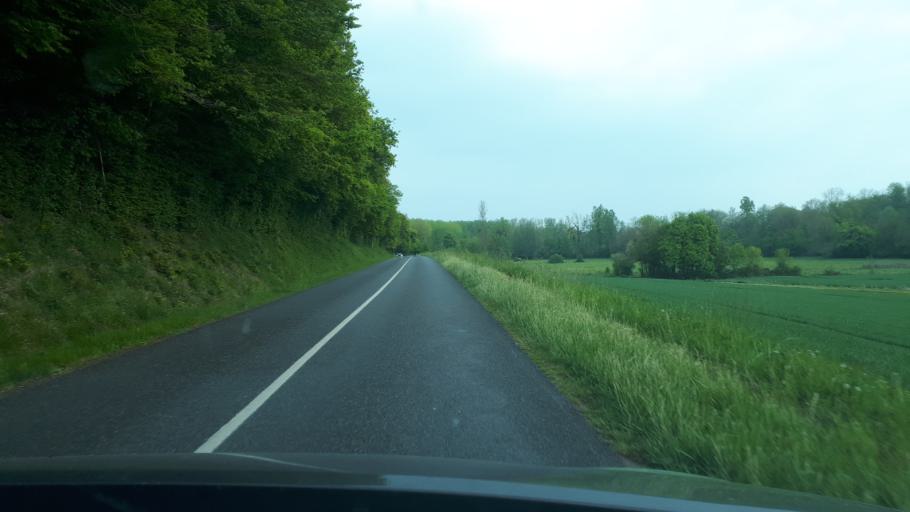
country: FR
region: Centre
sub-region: Departement du Loir-et-Cher
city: Lunay
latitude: 47.8188
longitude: 0.9500
